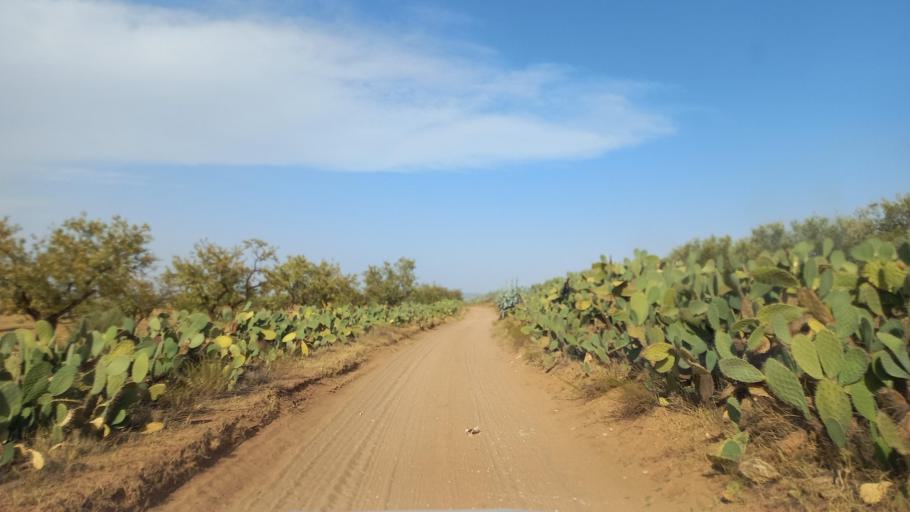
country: TN
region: Al Qasrayn
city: Kasserine
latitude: 35.2066
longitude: 8.9638
